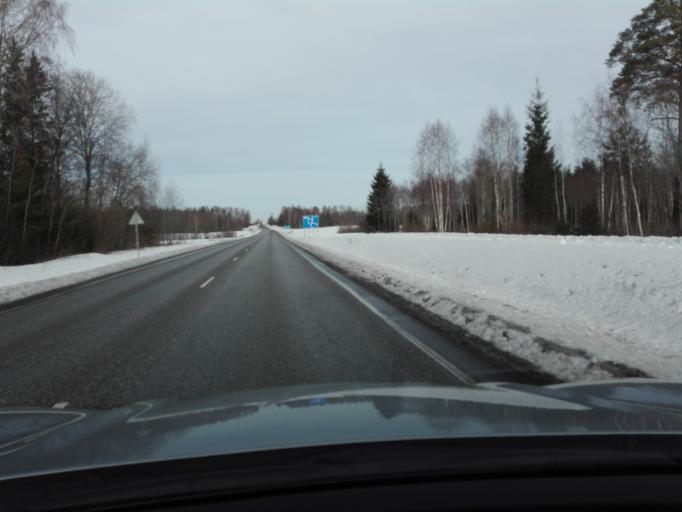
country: EE
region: Raplamaa
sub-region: Rapla vald
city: Rapla
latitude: 58.9851
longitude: 24.7837
